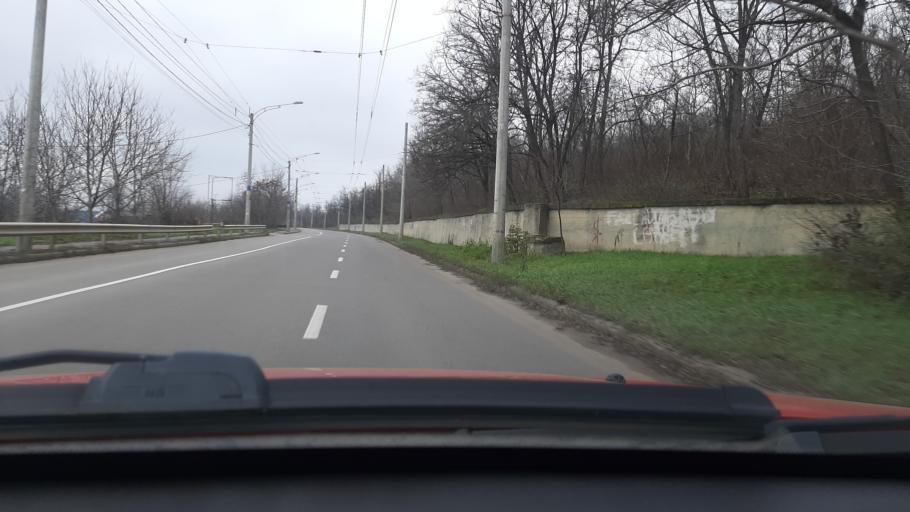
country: MD
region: Chisinau
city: Chisinau
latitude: 47.0524
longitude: 28.8197
